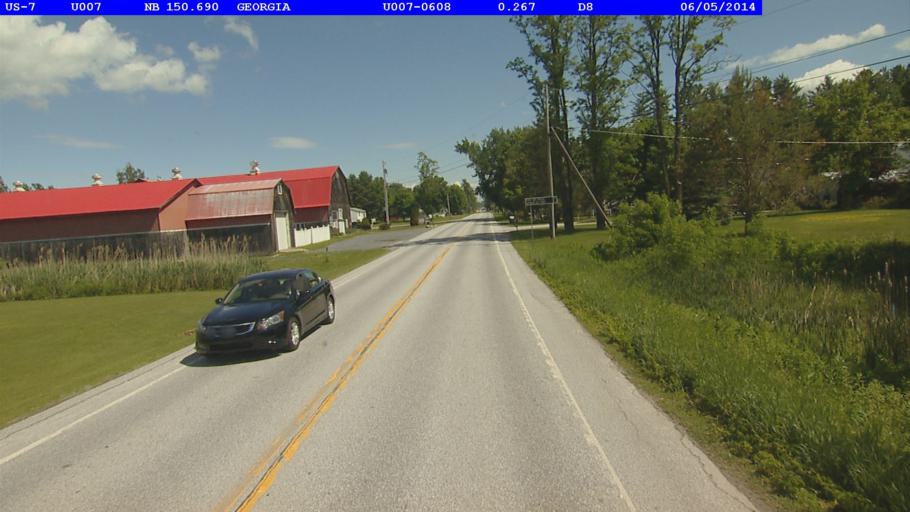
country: US
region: Vermont
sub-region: Chittenden County
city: Milton
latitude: 44.6830
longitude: -73.1113
